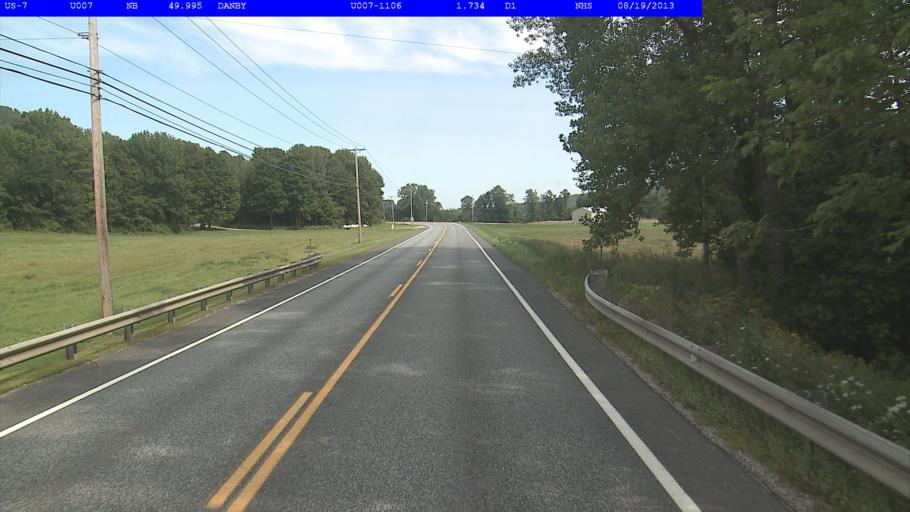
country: US
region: Vermont
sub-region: Rutland County
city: West Rutland
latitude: 43.3868
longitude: -72.9973
